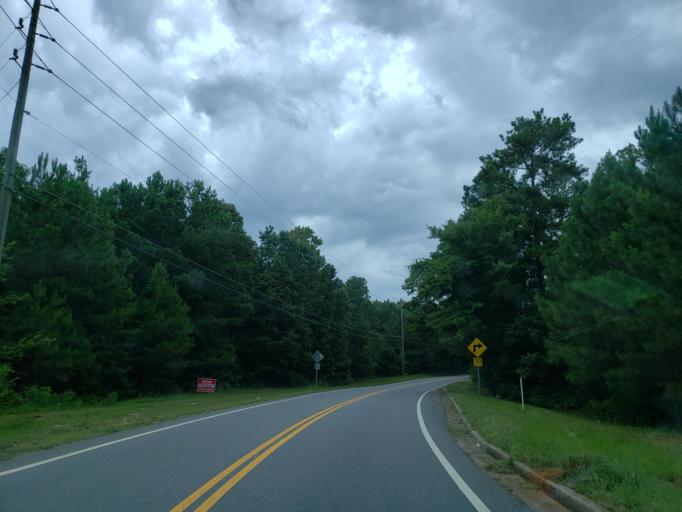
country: US
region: Georgia
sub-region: Paulding County
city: Dallas
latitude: 33.9953
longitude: -84.8044
